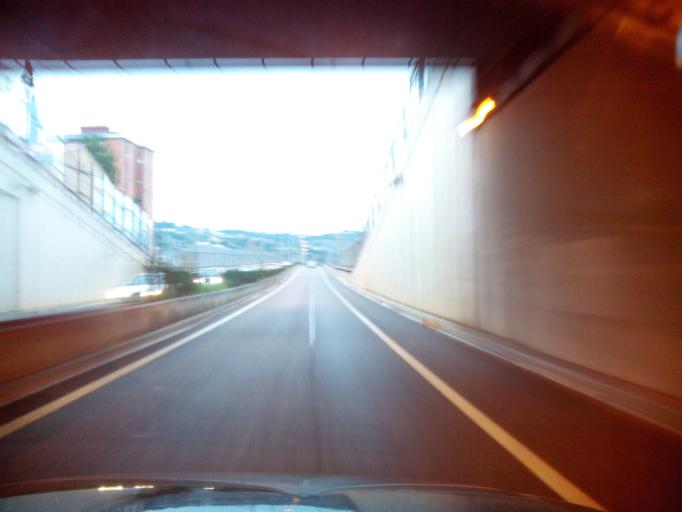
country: ES
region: Catalonia
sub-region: Provincia de Barcelona
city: Terrassa
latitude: 41.5508
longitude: 2.0193
